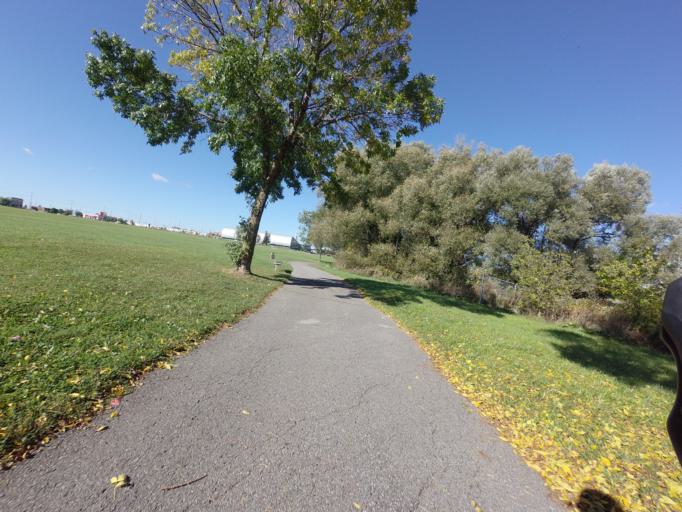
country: CA
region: Ontario
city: Ajax
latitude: 43.8577
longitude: -78.9401
